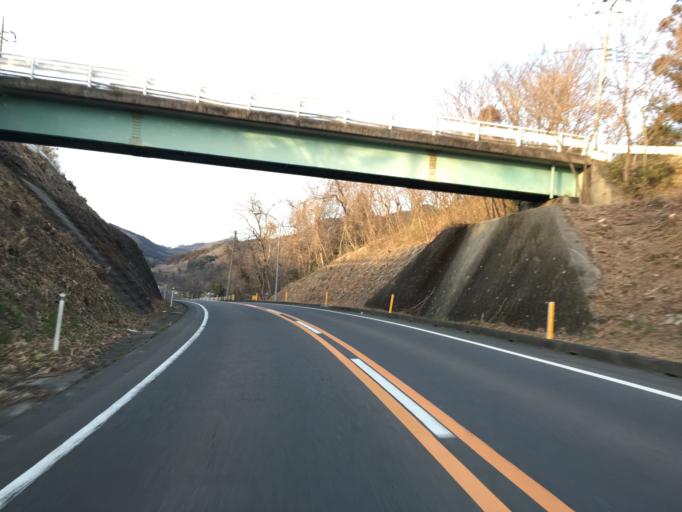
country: JP
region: Ibaraki
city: Daigo
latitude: 36.8194
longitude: 140.3788
